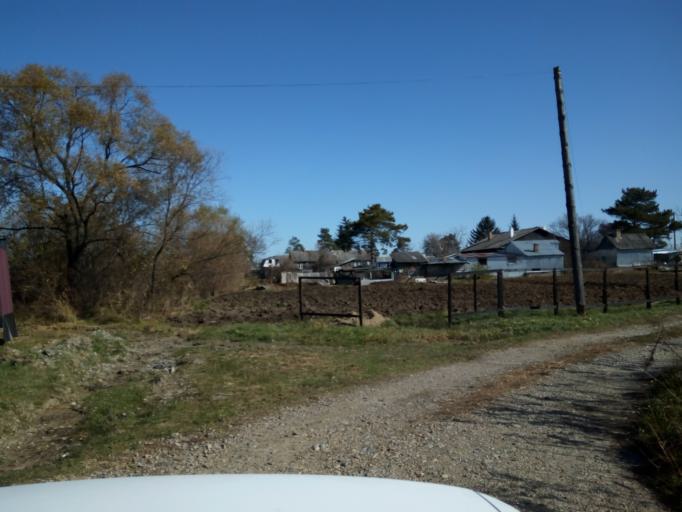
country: RU
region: Primorskiy
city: Dal'nerechensk
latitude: 45.9114
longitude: 133.7898
